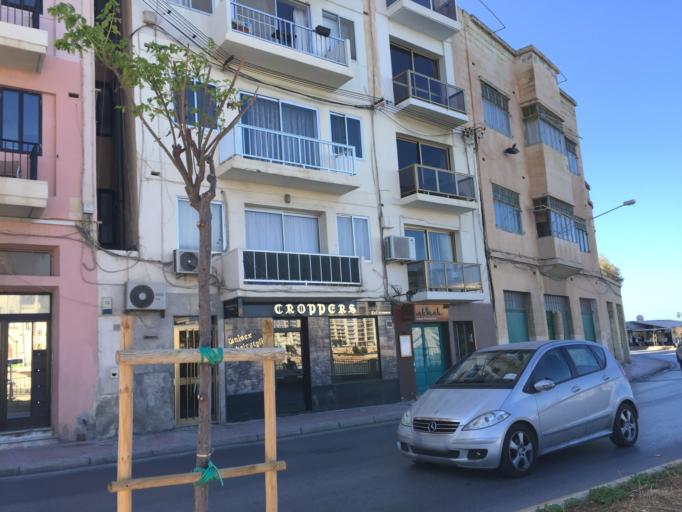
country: MT
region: Saint Julian
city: San Giljan
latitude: 35.9158
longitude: 14.4935
